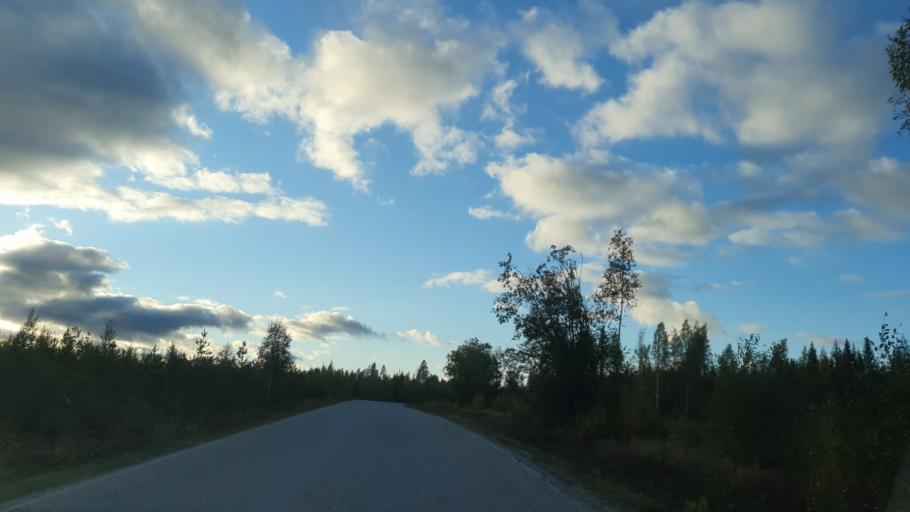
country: FI
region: Kainuu
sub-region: Kehys-Kainuu
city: Kuhmo
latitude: 63.9508
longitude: 29.7498
